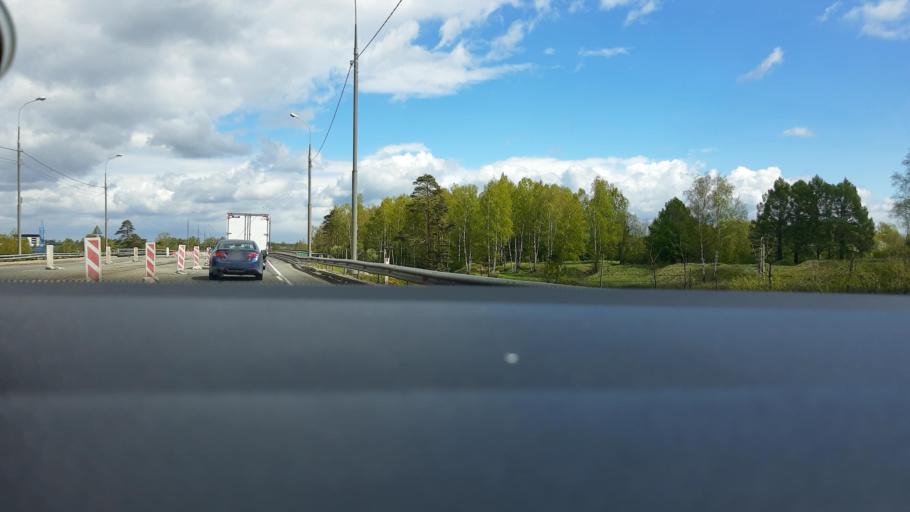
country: RU
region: Moskovskaya
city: Dedenevo
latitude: 56.2234
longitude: 37.5251
